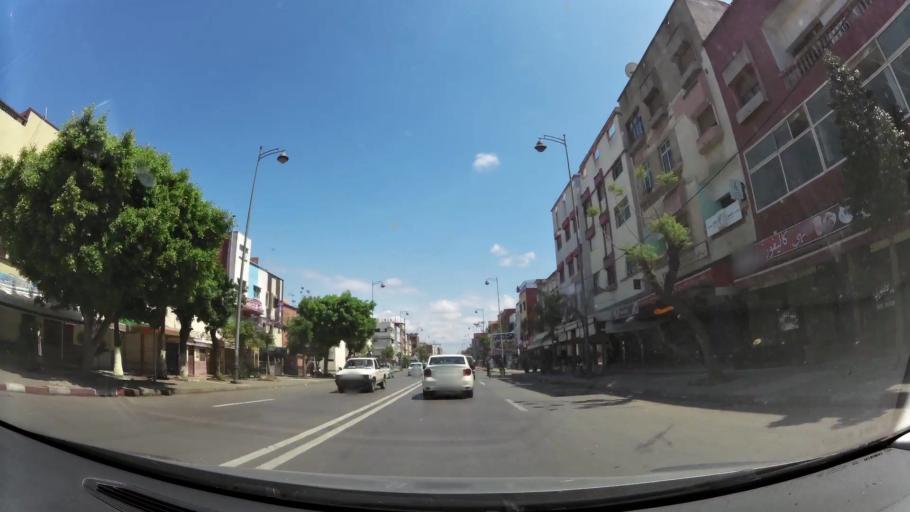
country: MA
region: Gharb-Chrarda-Beni Hssen
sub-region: Kenitra Province
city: Kenitra
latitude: 34.2476
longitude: -6.5541
